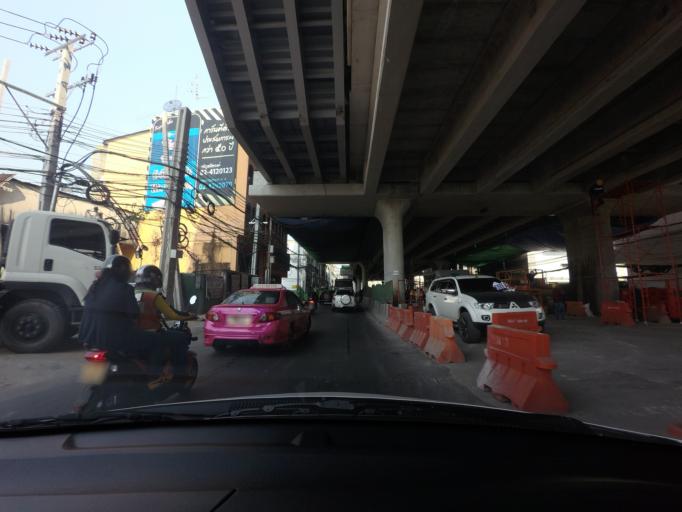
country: TH
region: Bangkok
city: Bangkok Noi
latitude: 13.7555
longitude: 100.4693
